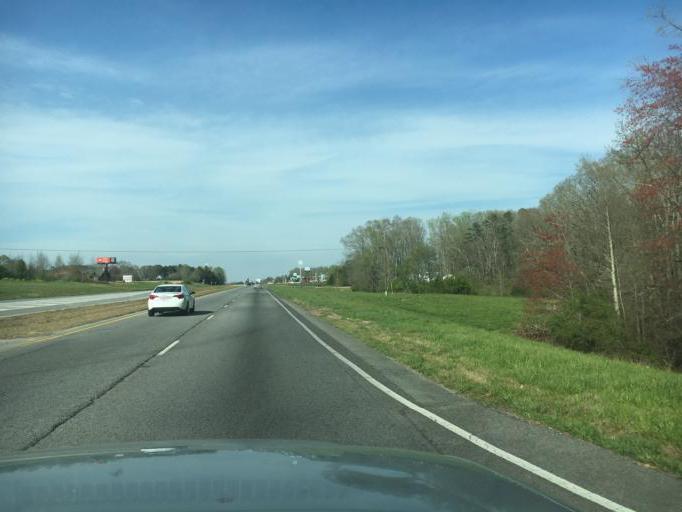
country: US
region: Georgia
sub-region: Banks County
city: Alto
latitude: 34.4803
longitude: -83.5873
